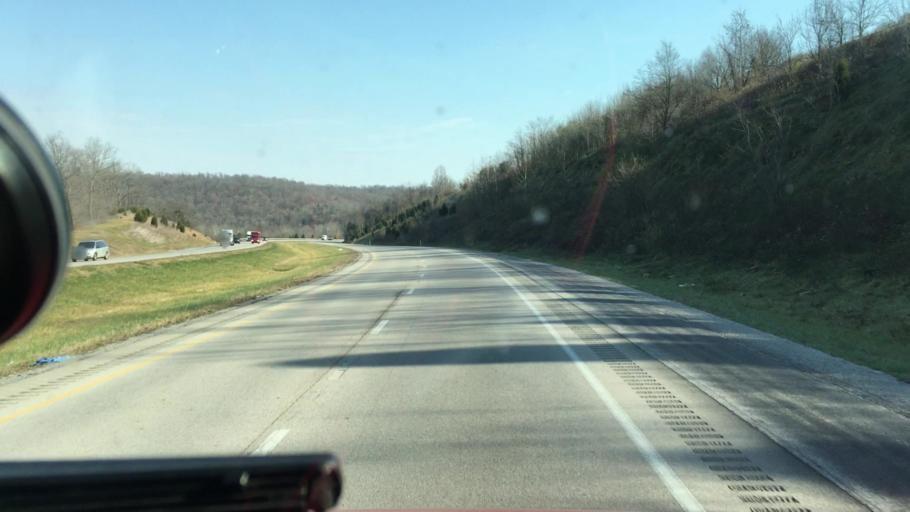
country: US
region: Kentucky
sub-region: Bath County
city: Owingsville
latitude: 38.1238
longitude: -83.7820
